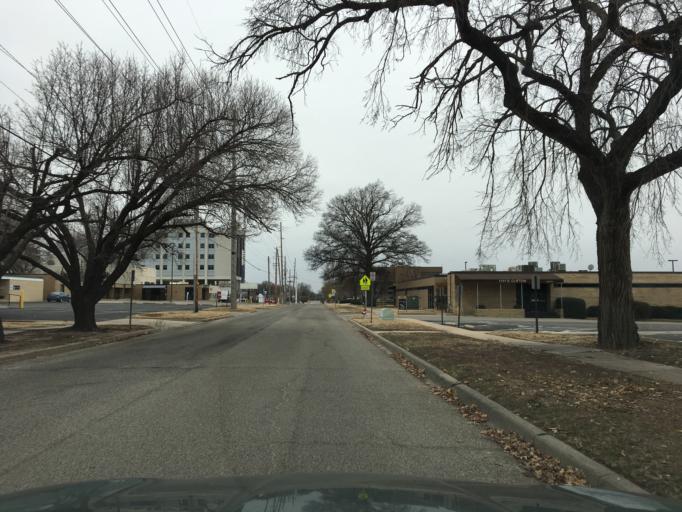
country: US
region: Kansas
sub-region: Sedgwick County
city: Wichita
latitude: 37.6681
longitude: -97.2943
